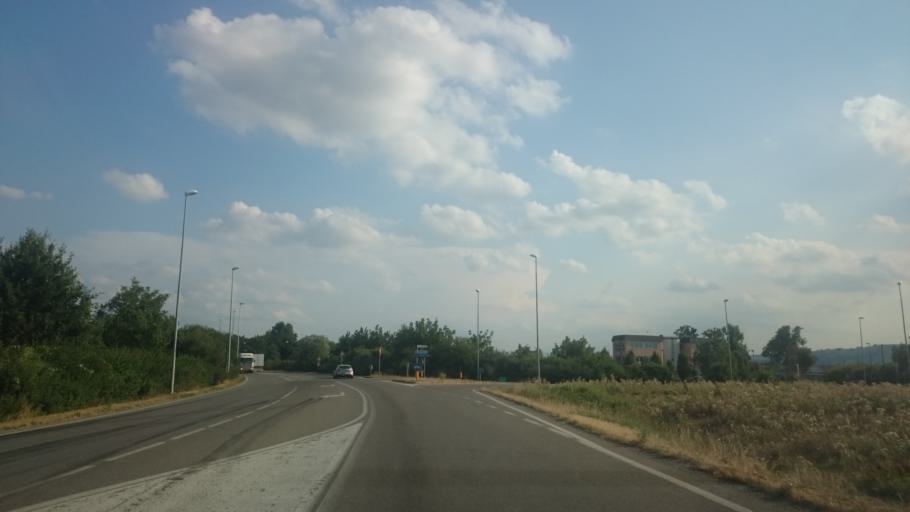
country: IT
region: Emilia-Romagna
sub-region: Provincia di Reggio Emilia
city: Salvaterra
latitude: 44.6058
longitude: 10.7765
